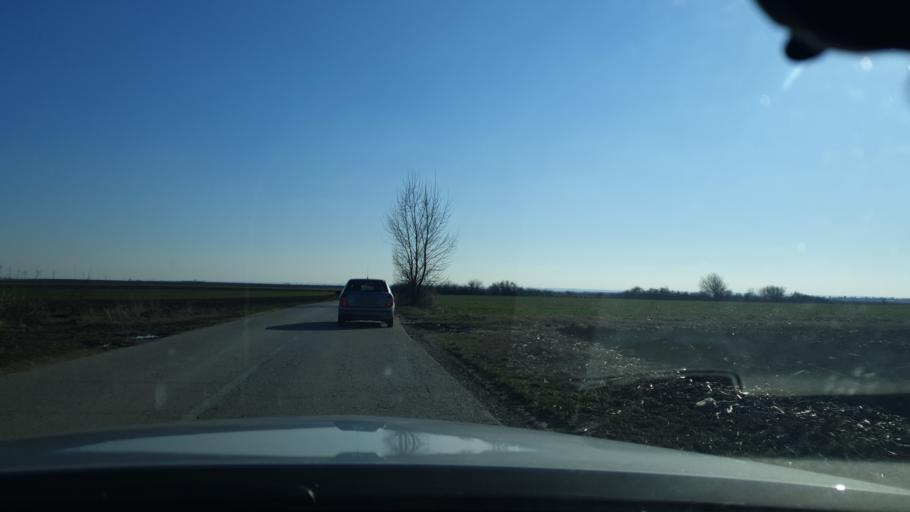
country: RS
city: Vrdnik
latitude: 45.0718
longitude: 19.8092
